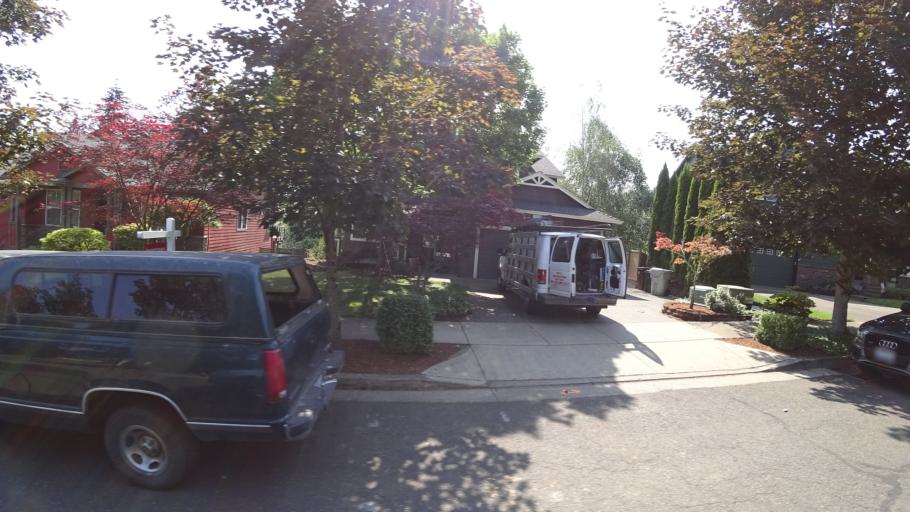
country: US
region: Oregon
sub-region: Clackamas County
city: Happy Valley
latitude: 45.4415
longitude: -122.5353
